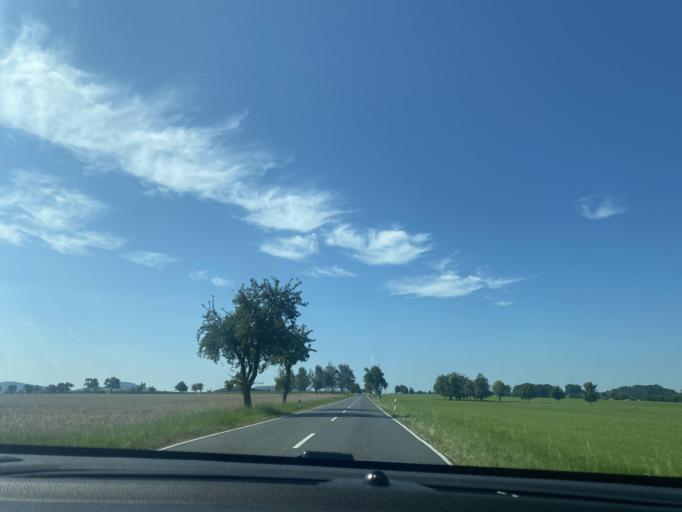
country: DE
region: Saxony
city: Bernstadt
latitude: 51.0233
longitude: 14.8058
